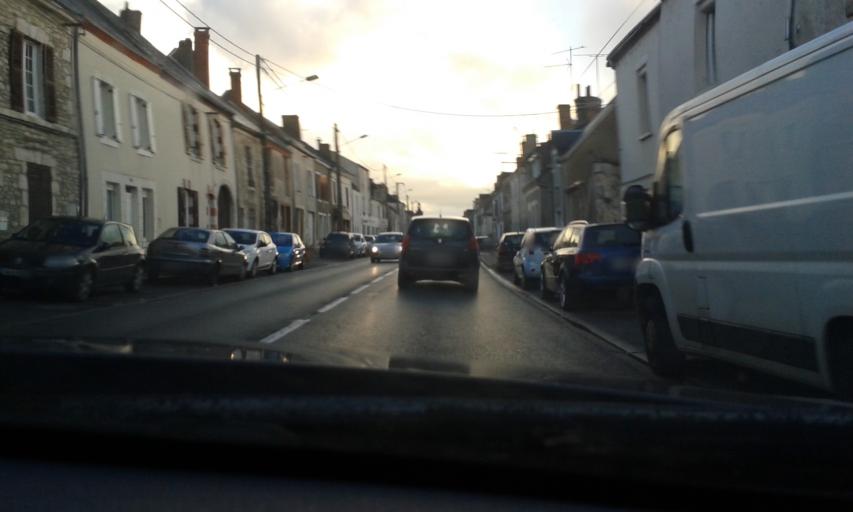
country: FR
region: Centre
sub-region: Departement du Loiret
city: Chevilly
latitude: 48.0296
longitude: 1.8745
